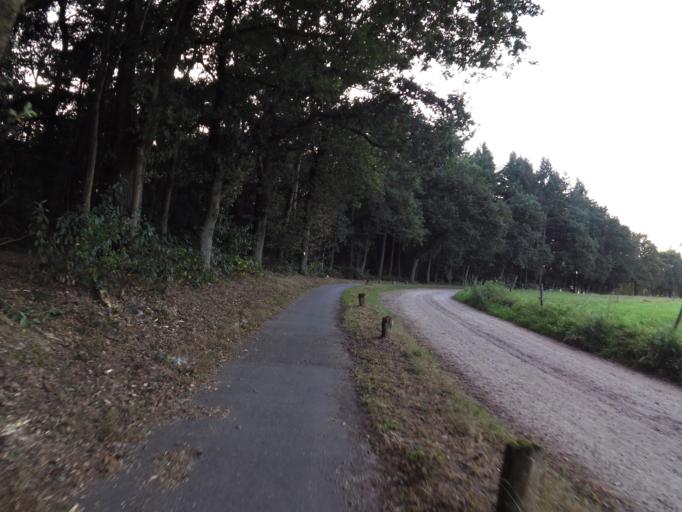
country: NL
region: Gelderland
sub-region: Gemeente Nijmegen
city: Lindenholt
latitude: 51.7955
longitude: 5.7944
